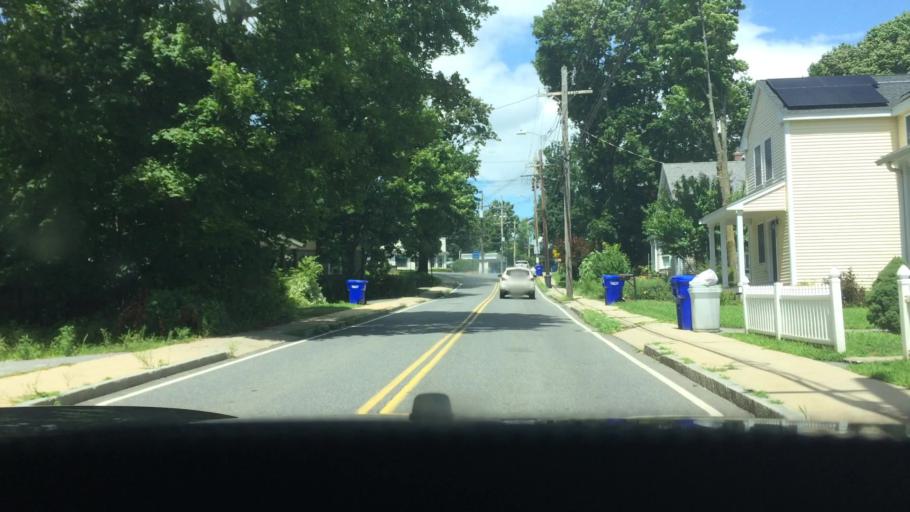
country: US
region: Massachusetts
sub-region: Middlesex County
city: Maynard
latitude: 42.4346
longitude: -71.4511
